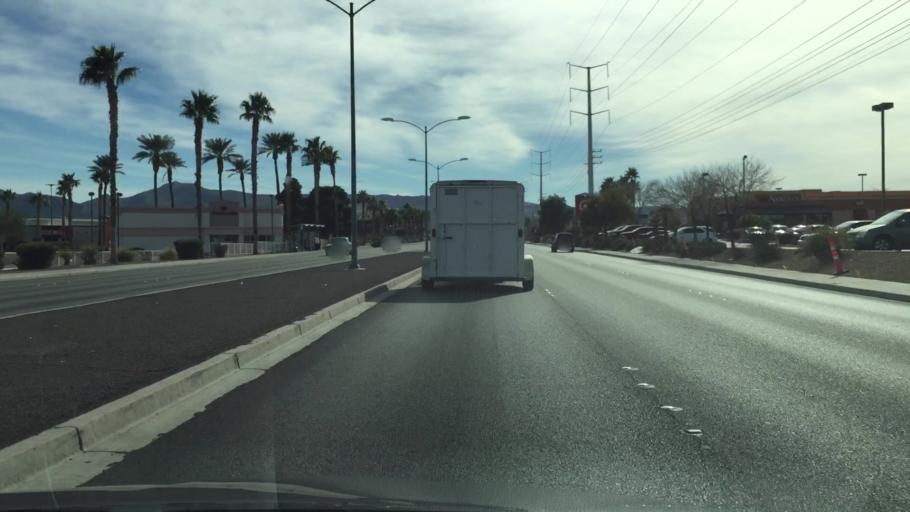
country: US
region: Nevada
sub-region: Clark County
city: Whitney
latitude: 36.0667
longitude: -115.0462
